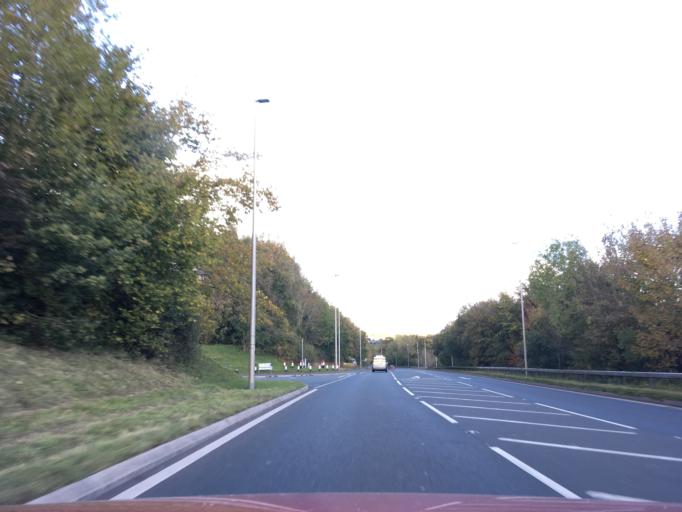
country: GB
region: Wales
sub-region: Sir Powys
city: Brecon
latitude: 51.9418
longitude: -3.4146
